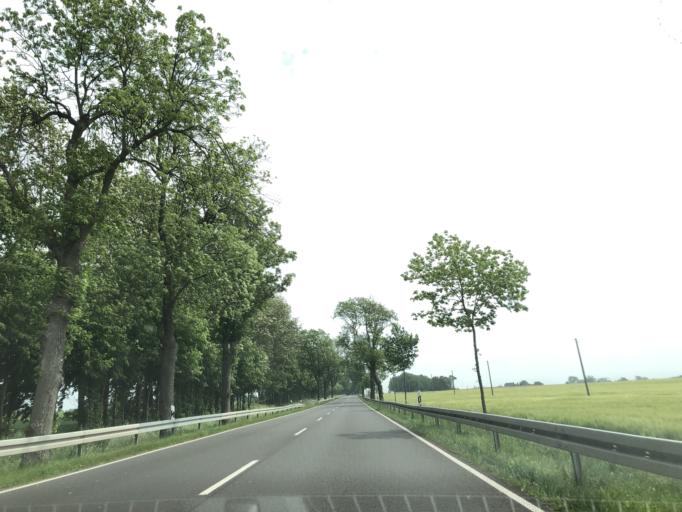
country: DE
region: Brandenburg
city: Kyritz
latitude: 52.9654
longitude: 12.3258
